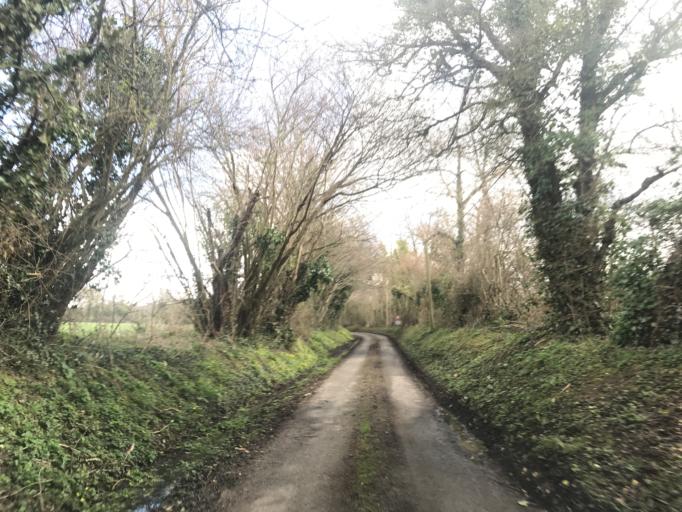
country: FR
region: Lower Normandy
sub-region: Departement du Calvados
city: Dives-sur-Mer
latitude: 49.2670
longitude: -0.0969
